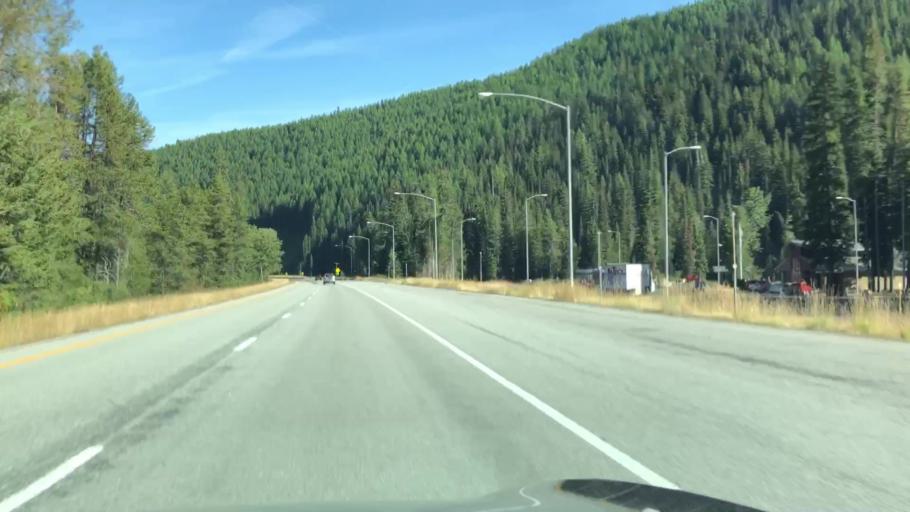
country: US
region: Idaho
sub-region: Shoshone County
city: Wallace
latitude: 47.4205
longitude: -115.6298
